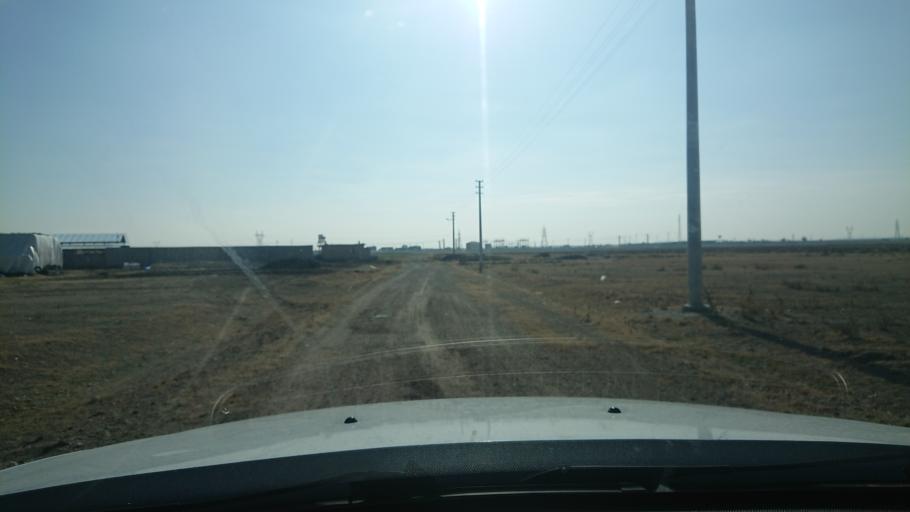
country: TR
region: Aksaray
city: Sultanhani
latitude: 38.2598
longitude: 33.4719
